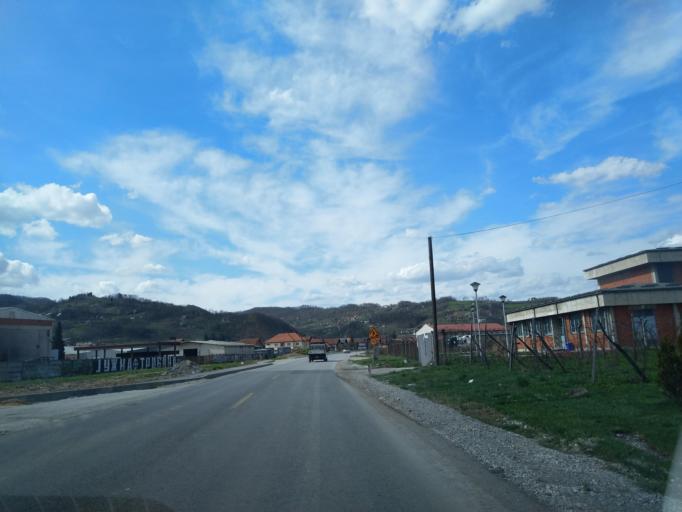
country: RS
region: Central Serbia
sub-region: Zlatiborski Okrug
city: Arilje
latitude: 43.7571
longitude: 20.0999
